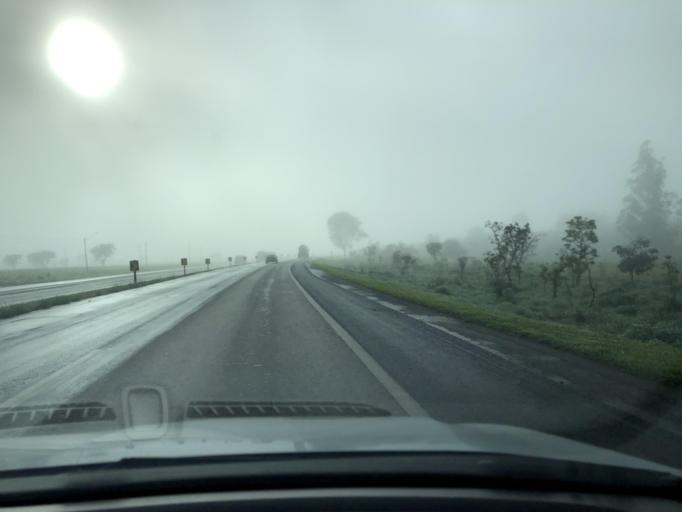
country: BR
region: Goias
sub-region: Luziania
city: Luziania
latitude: -16.2775
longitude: -47.8630
